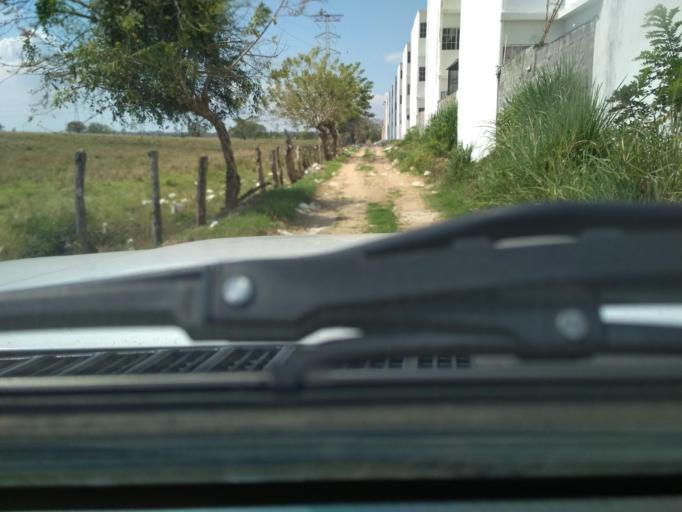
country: MX
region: Veracruz
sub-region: Veracruz
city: Las Amapolas
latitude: 19.1370
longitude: -96.2209
